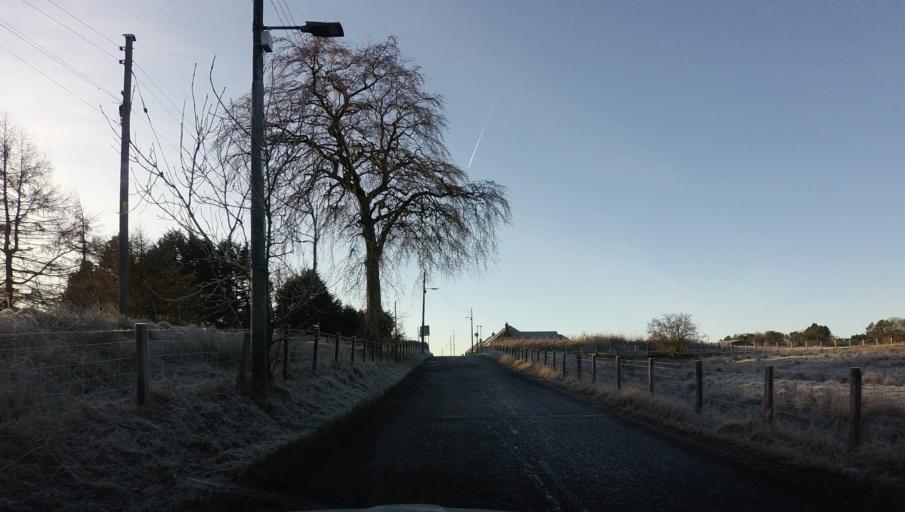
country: GB
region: Scotland
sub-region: North Lanarkshire
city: Shotts
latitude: 55.8144
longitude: -3.8344
